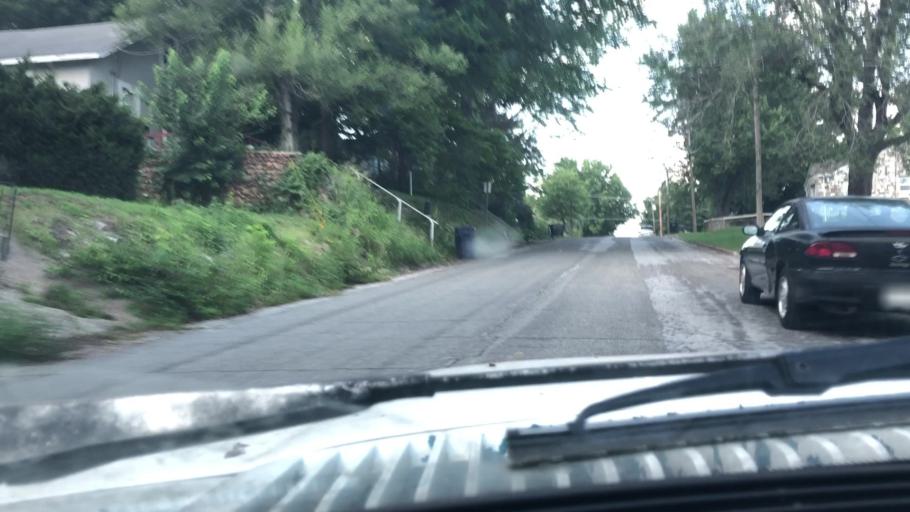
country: US
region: Missouri
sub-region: Newton County
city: Neosho
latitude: 36.8631
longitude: -94.3663
